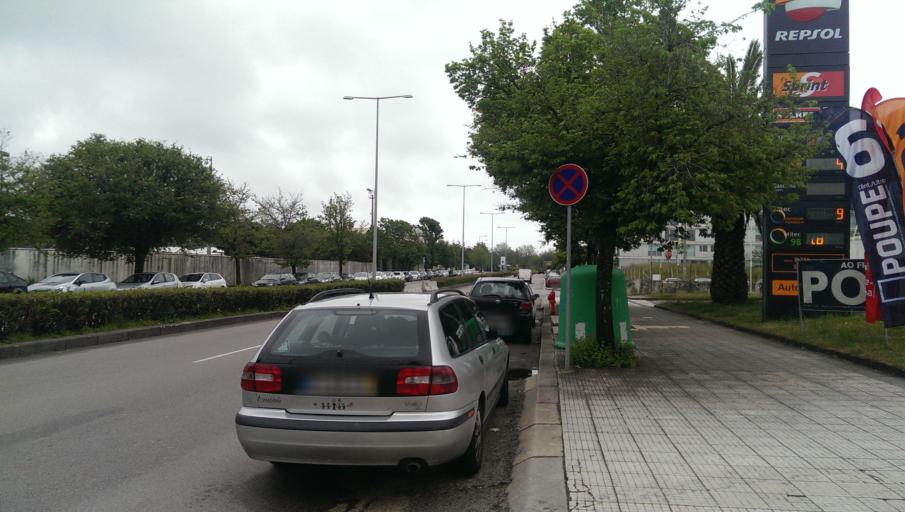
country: PT
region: Porto
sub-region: Matosinhos
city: Matosinhos
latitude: 41.1752
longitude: -8.6811
